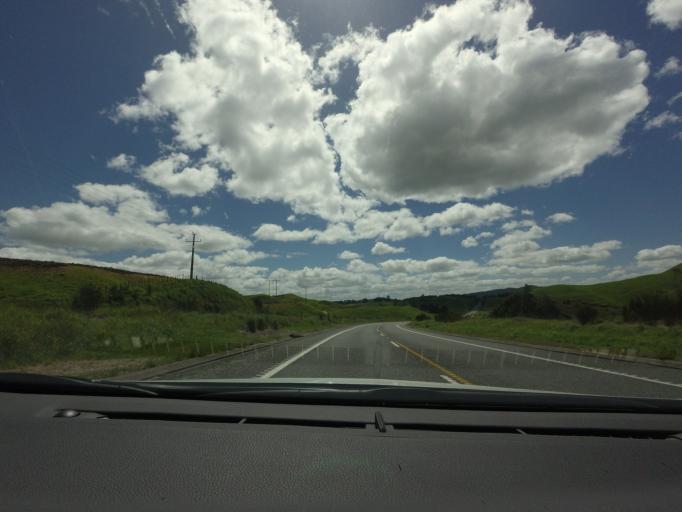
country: NZ
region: Bay of Plenty
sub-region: Rotorua District
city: Rotorua
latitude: -38.2632
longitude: 176.3213
